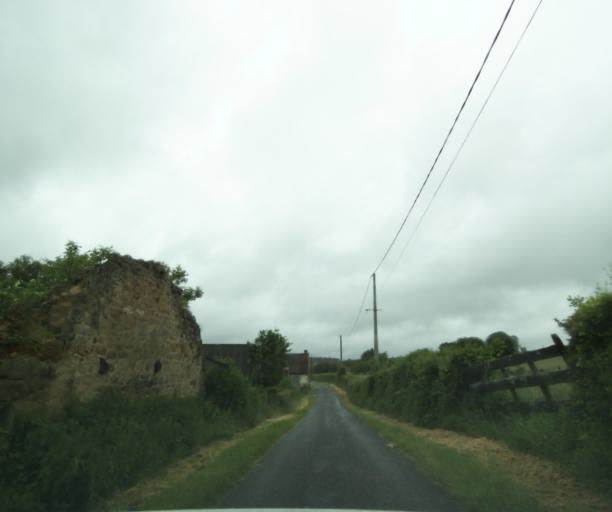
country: FR
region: Bourgogne
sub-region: Departement de Saone-et-Loire
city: Charolles
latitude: 46.4815
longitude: 4.4127
